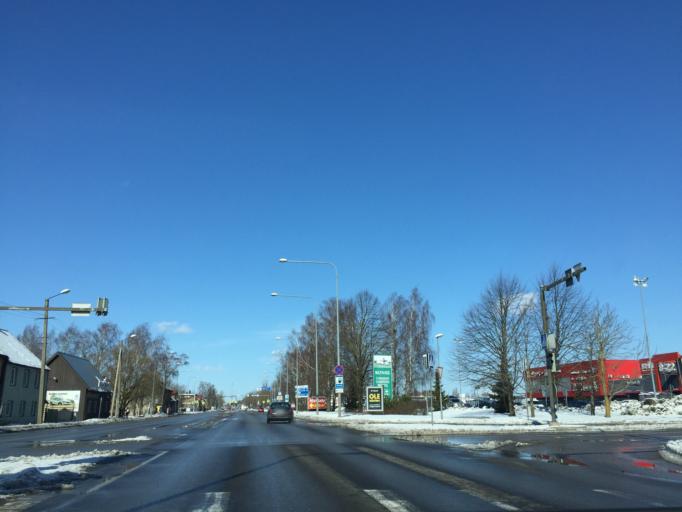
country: EE
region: Paernumaa
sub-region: Paernu linn
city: Parnu
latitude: 58.3685
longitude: 24.5508
